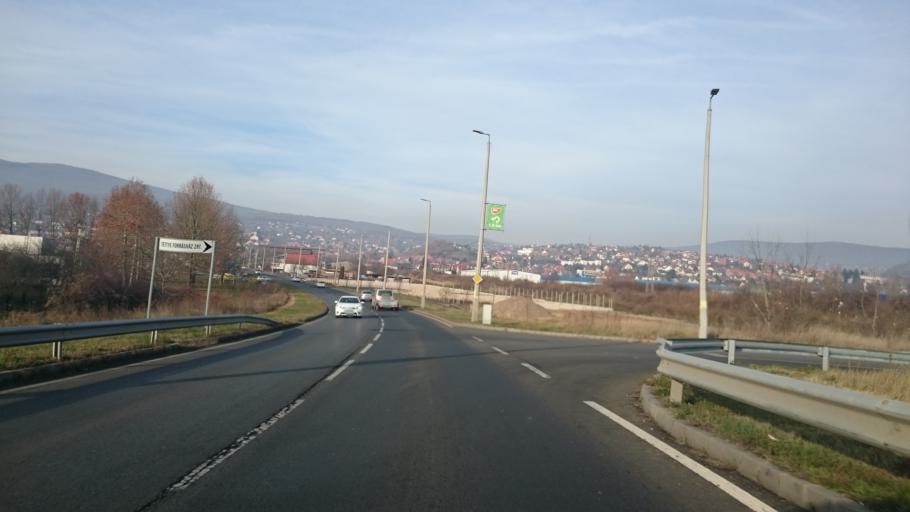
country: HU
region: Baranya
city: Pellerd
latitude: 46.0601
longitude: 18.1756
